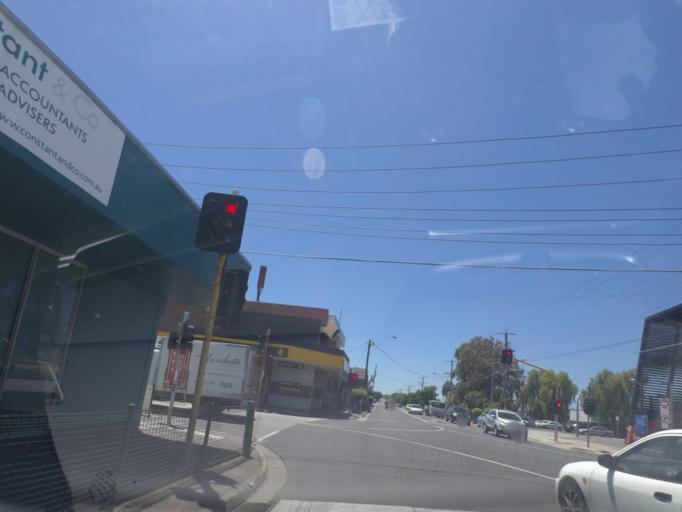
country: AU
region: Victoria
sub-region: Whittlesea
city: Thomastown
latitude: -37.6804
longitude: 145.0137
